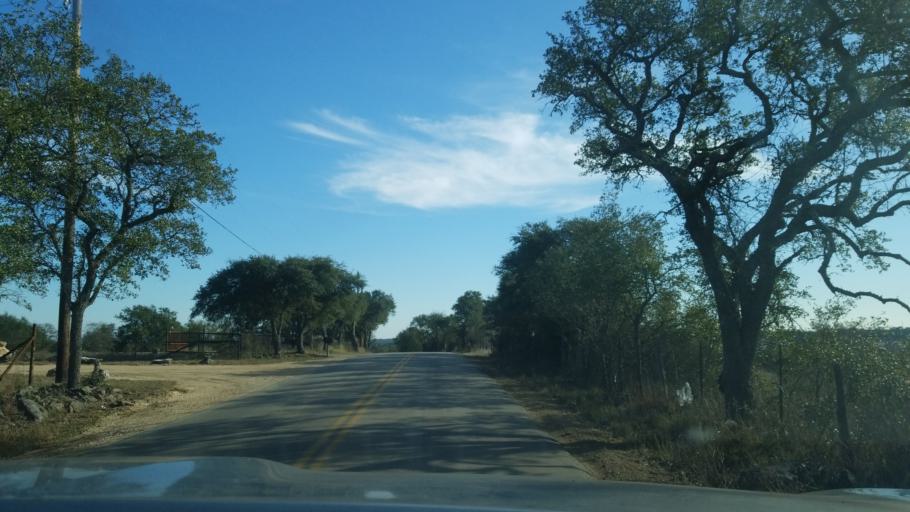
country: US
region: Texas
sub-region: Comal County
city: Canyon Lake
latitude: 29.7859
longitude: -98.2852
